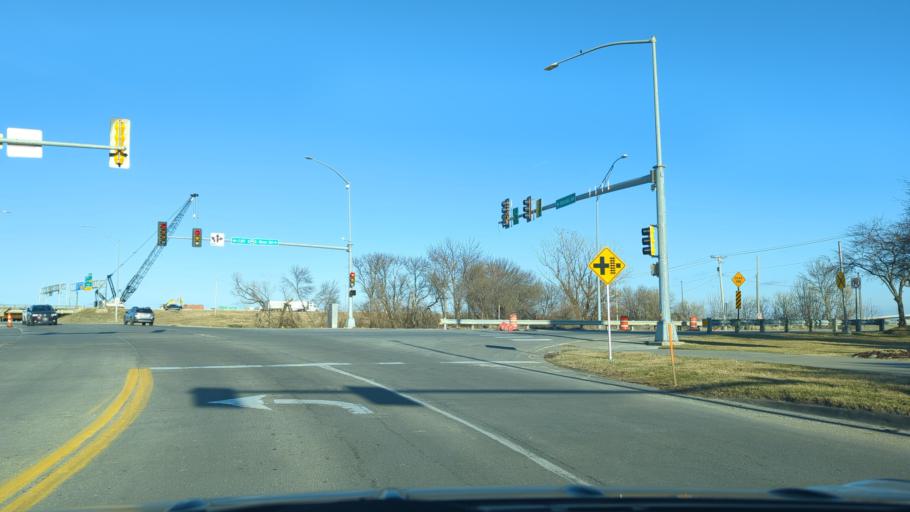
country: US
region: Nebraska
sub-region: Douglas County
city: Omaha
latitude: 41.2411
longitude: -95.9074
